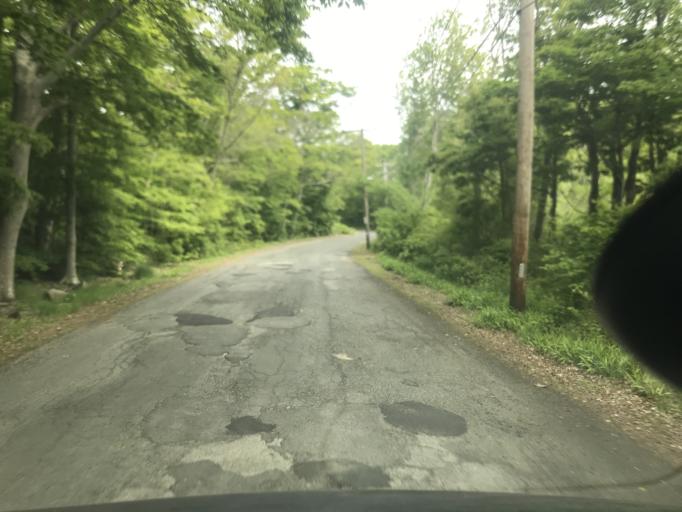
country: US
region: Massachusetts
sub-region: Essex County
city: Rockport
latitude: 42.6609
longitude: -70.6310
